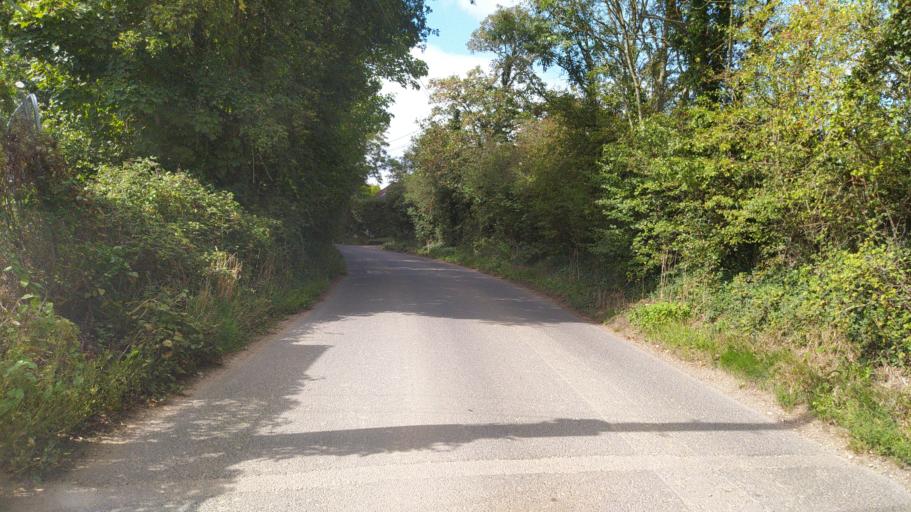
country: GB
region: England
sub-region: Hampshire
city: Romsey
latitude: 51.0085
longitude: -1.5190
